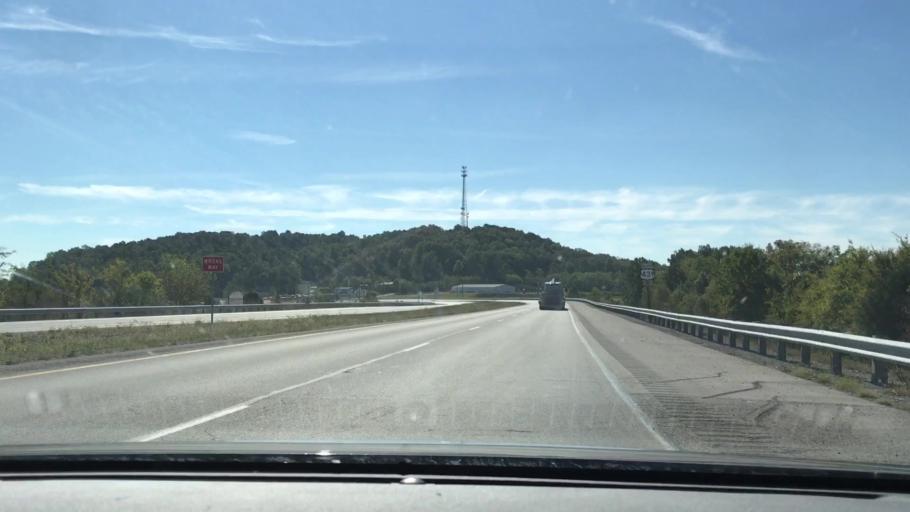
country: US
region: Kentucky
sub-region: Logan County
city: Russellville
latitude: 36.8392
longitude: -86.9186
